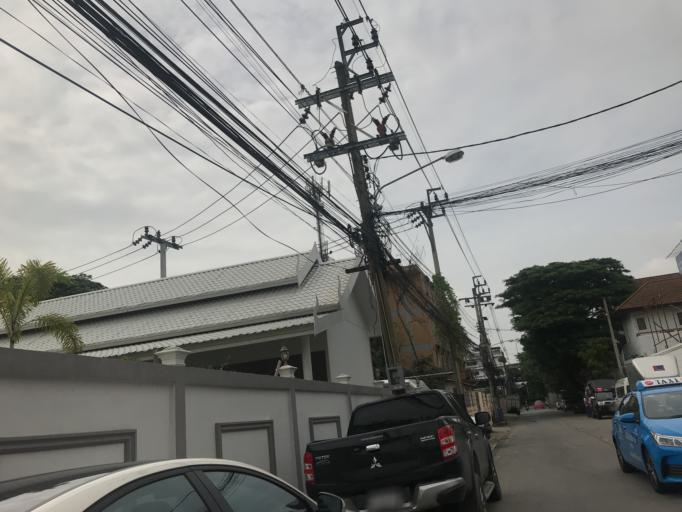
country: TH
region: Bangkok
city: Suan Luang
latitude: 13.7448
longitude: 100.6358
